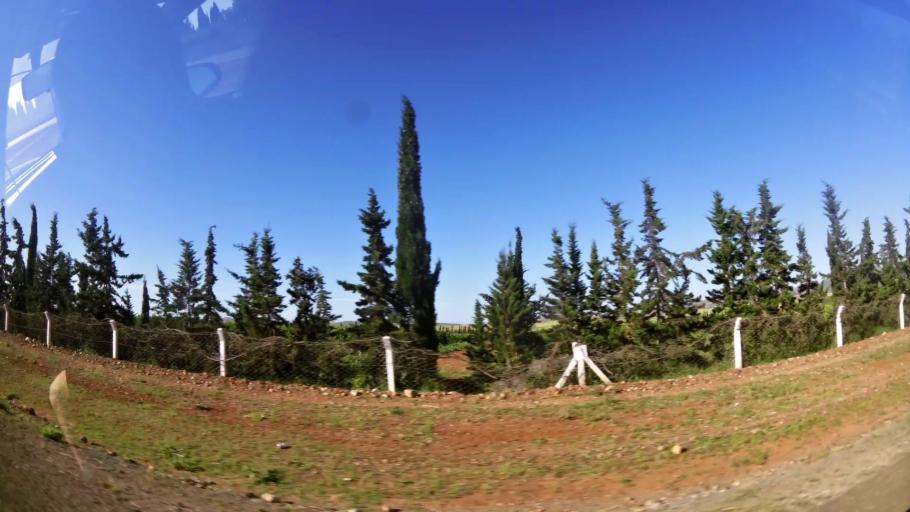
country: MA
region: Oriental
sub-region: Berkane-Taourirt
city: Ahfir
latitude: 34.9999
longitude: -2.1742
